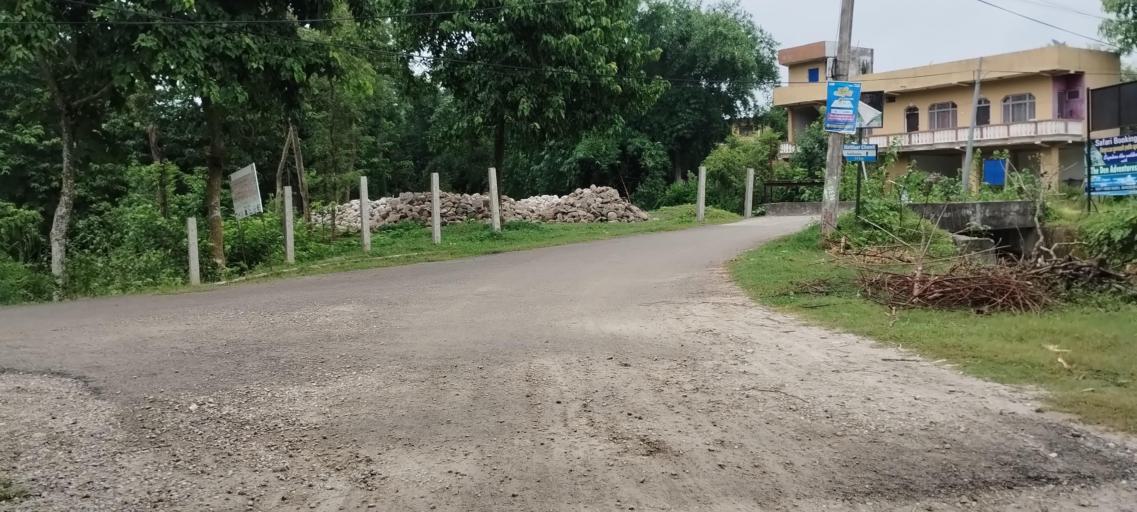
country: NP
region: Far Western
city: Tikapur
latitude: 28.4514
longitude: 81.2438
